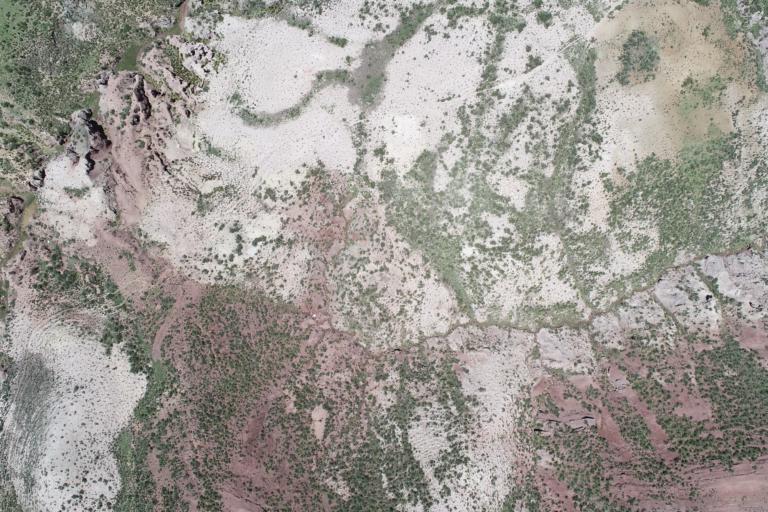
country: BO
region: La Paz
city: Patacamaya
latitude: -17.2711
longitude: -68.5043
